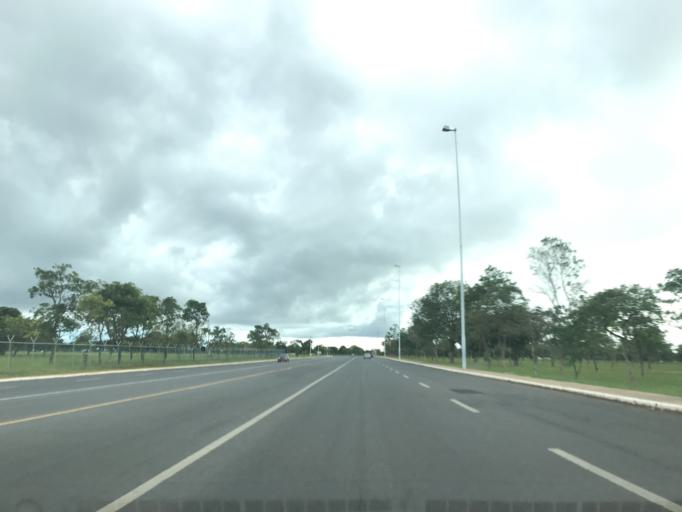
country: BR
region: Federal District
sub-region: Brasilia
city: Brasilia
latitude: -15.7764
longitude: -47.9212
